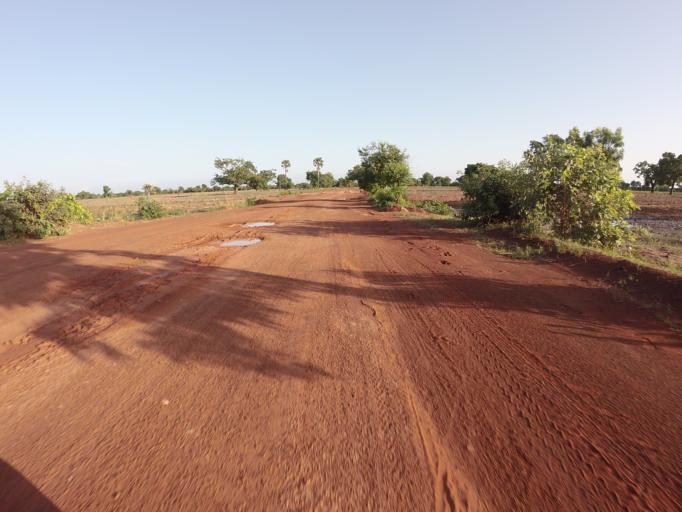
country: TG
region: Savanes
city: Sansanne-Mango
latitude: 10.3460
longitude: -0.0926
